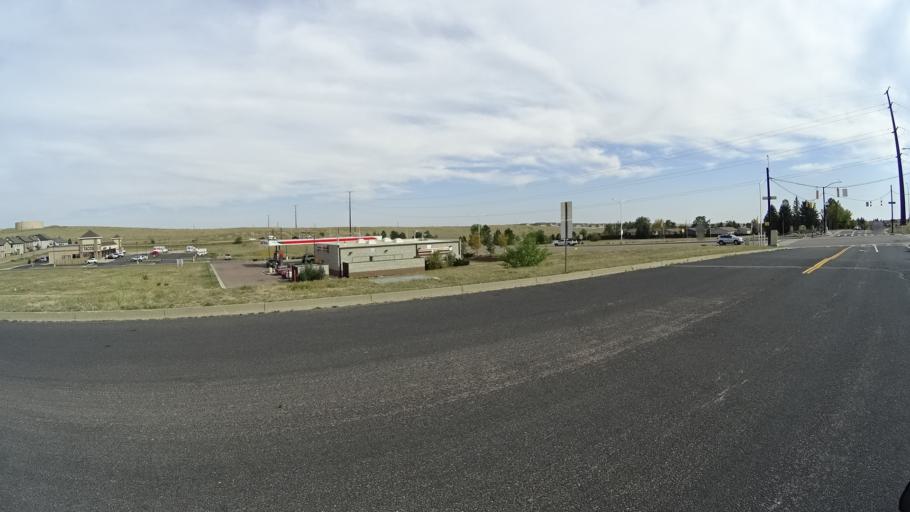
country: US
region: Colorado
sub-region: El Paso County
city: Cimarron Hills
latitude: 38.9016
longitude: -104.6866
